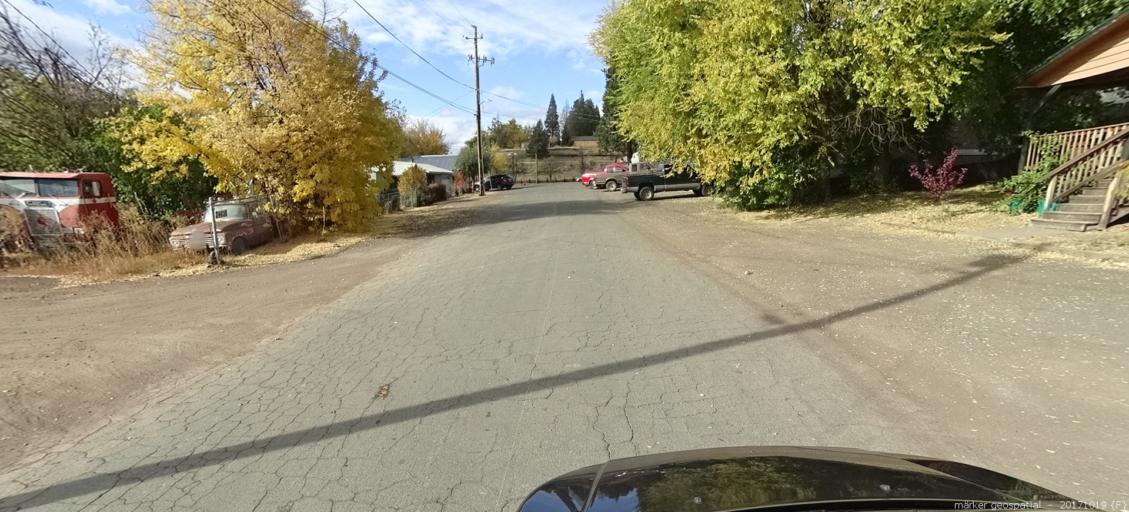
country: US
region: California
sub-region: Shasta County
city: Burney
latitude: 41.0024
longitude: -121.4393
